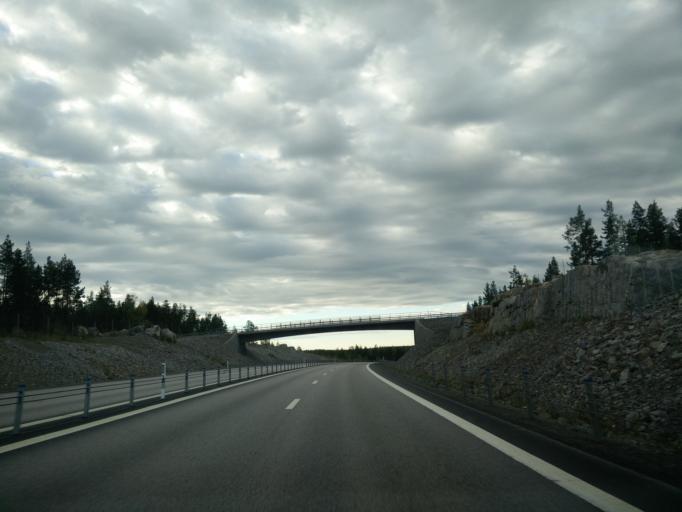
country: SE
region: Gaevleborg
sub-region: Hudiksvalls Kommun
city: Iggesund
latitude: 61.6947
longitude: 17.0571
